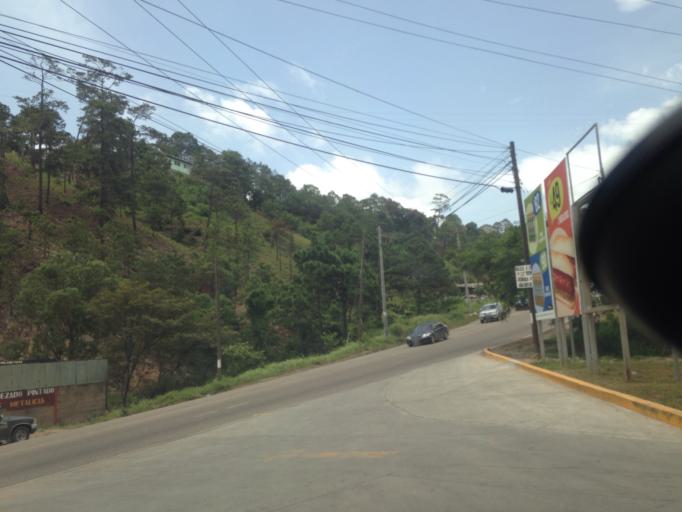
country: HN
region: Francisco Morazan
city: El Tablon
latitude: 14.0472
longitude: -87.1545
